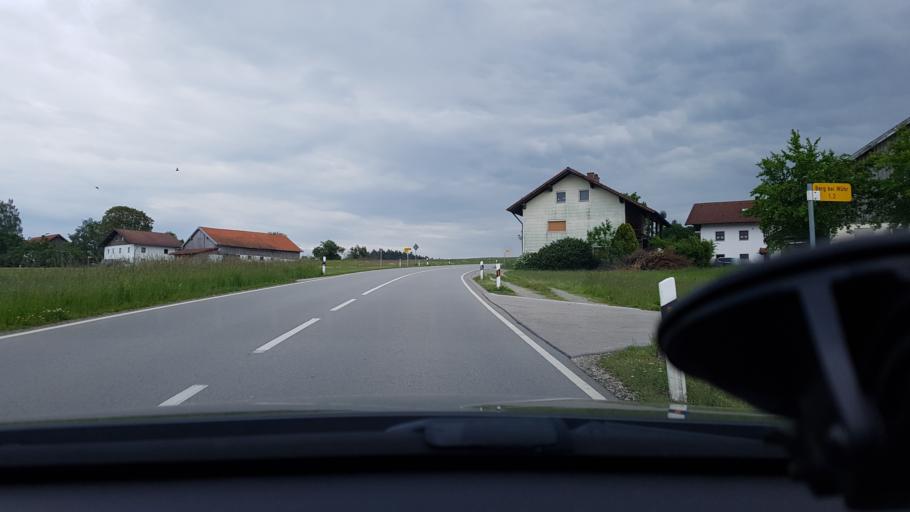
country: DE
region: Bavaria
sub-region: Lower Bavaria
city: Pfarrkirchen
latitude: 48.4128
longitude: 12.9631
